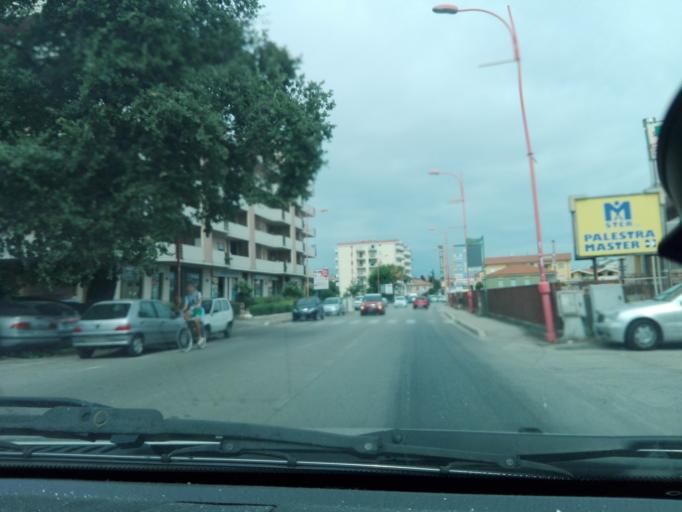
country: IT
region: Abruzzo
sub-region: Provincia di Pescara
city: Montesilvano Marina
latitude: 42.4958
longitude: 14.1715
